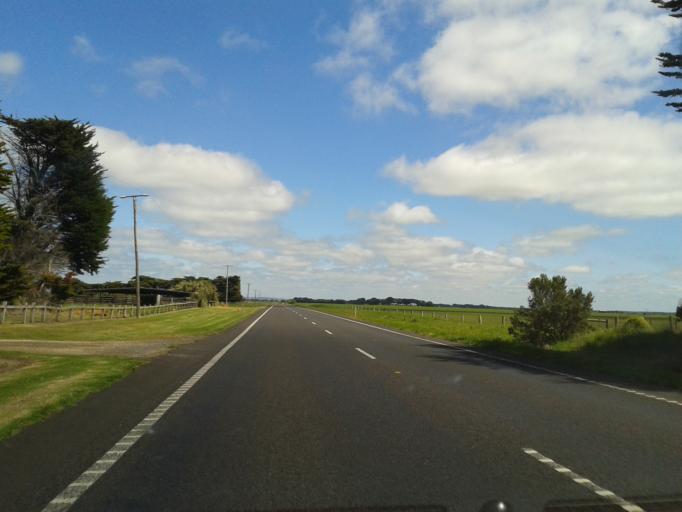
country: AU
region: Victoria
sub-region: Moyne
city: Port Fairy
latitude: -38.2781
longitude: 141.9969
